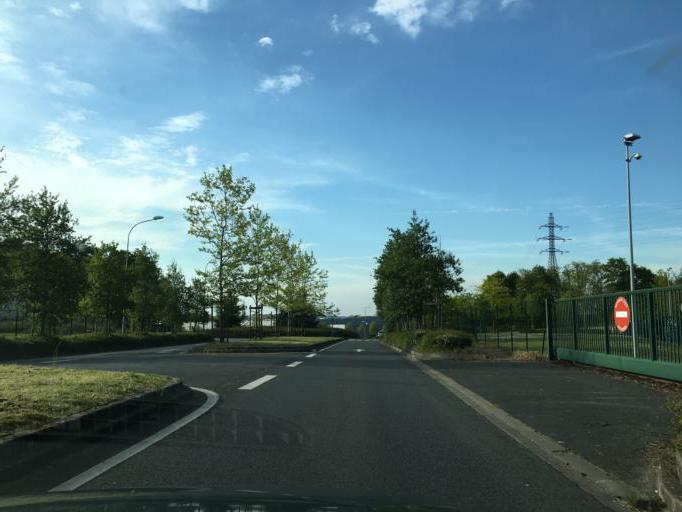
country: FR
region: Centre
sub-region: Departement du Loiret
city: Ingre
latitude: 47.9371
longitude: 1.8409
